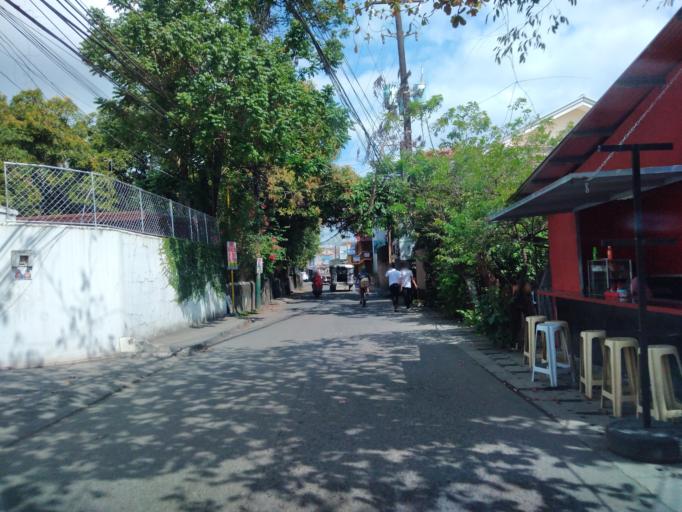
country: PH
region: Central Luzon
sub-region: Province of Bulacan
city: Santa Maria
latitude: 14.8212
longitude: 120.9630
